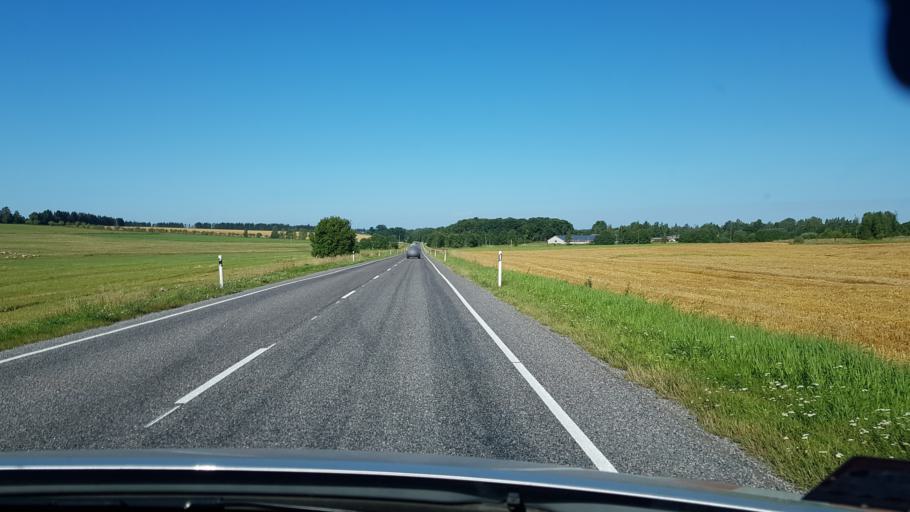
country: EE
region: Tartu
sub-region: Tartu linn
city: Tartu
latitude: 58.4657
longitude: 26.7452
